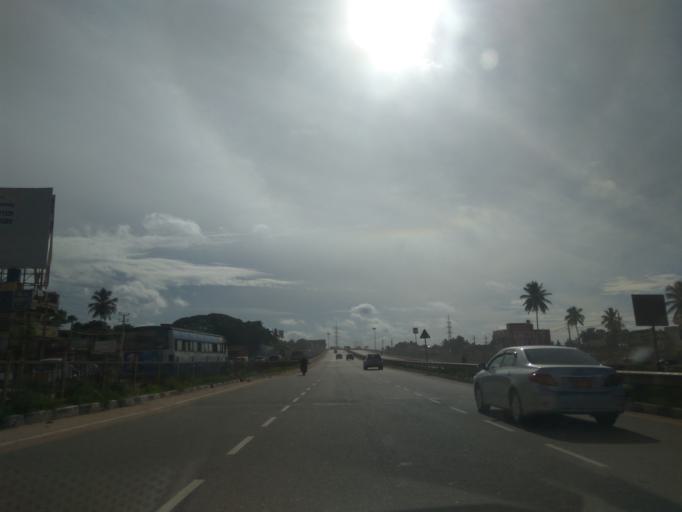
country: IN
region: Karnataka
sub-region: Bangalore Rural
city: Hoskote
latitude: 13.0774
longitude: 77.7972
